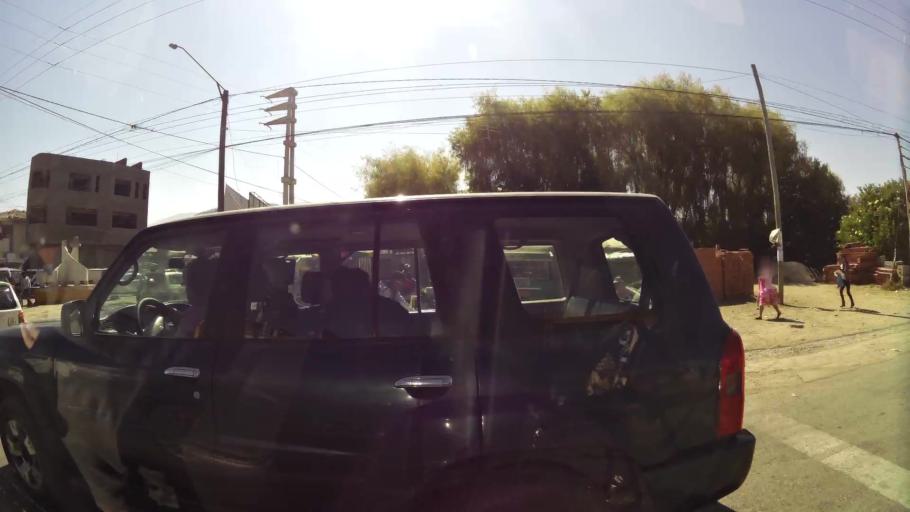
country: PE
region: Junin
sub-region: Provincia de Huancayo
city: San Agustin
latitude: -11.9956
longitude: -75.2550
